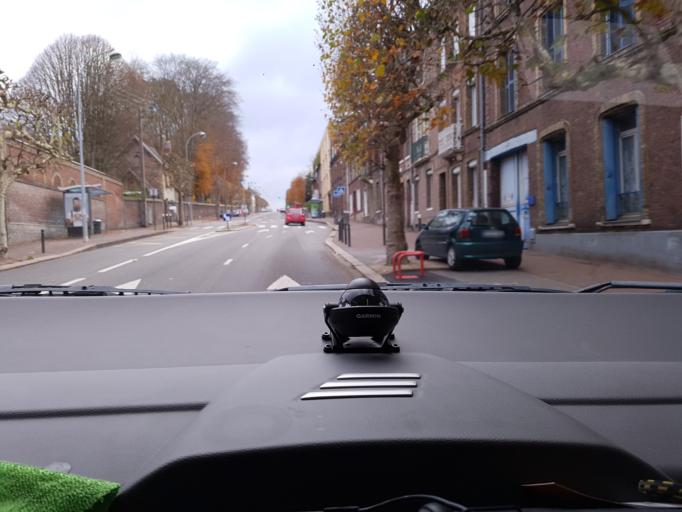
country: FR
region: Haute-Normandie
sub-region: Departement de la Seine-Maritime
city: Rouxmesnil-Bouteilles
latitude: 49.9194
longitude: 1.0737
